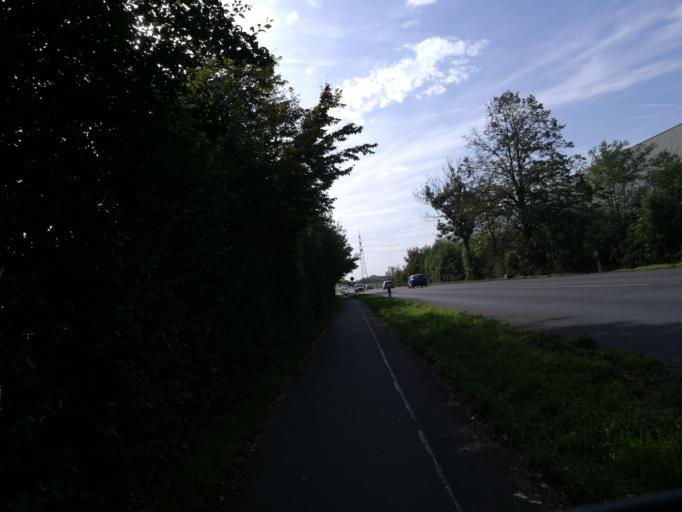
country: DE
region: North Rhine-Westphalia
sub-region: Regierungsbezirk Dusseldorf
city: Dusseldorf
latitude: 51.1533
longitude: 6.7646
